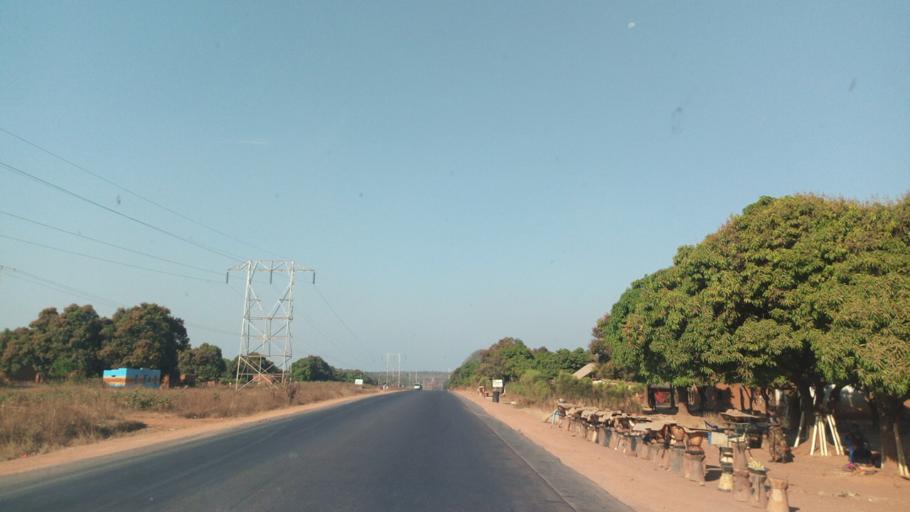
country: CD
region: Katanga
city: Likasi
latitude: -11.0009
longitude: 26.8769
